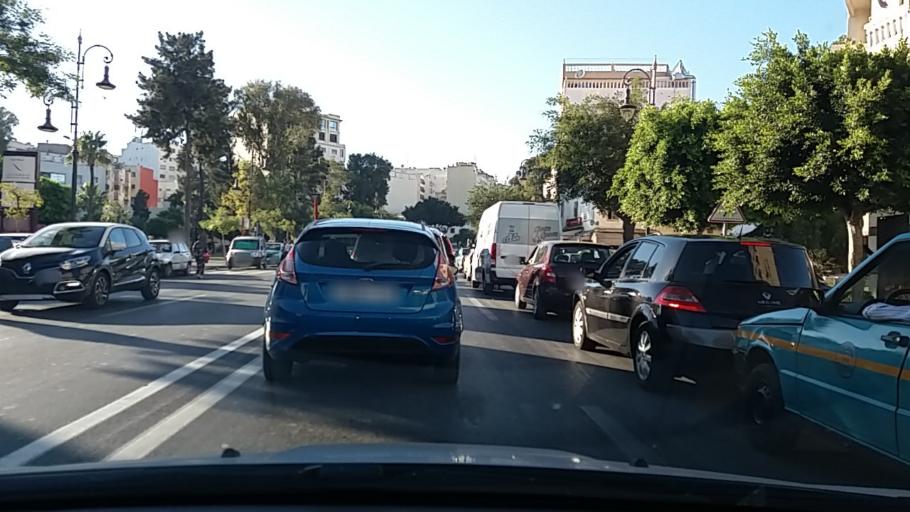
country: MA
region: Tanger-Tetouan
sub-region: Tanger-Assilah
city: Tangier
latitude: 35.7757
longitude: -5.8184
